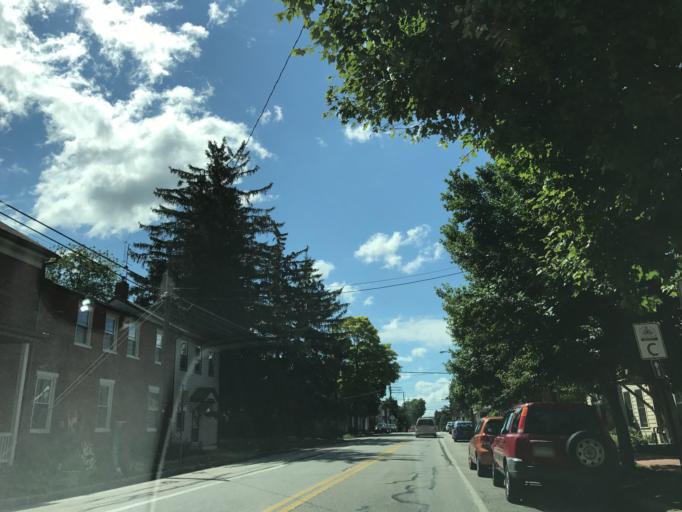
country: US
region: Pennsylvania
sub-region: Lancaster County
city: Maytown
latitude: 40.0753
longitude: -76.5820
